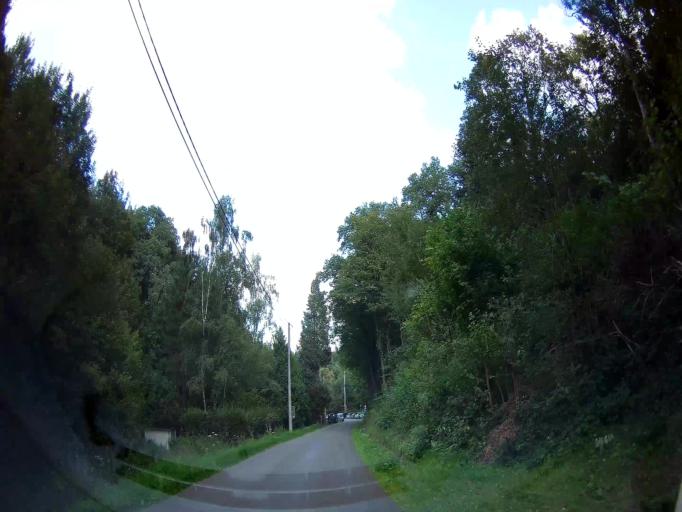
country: BE
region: Wallonia
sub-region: Province de Namur
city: Onhaye
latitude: 50.2900
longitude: 4.8004
